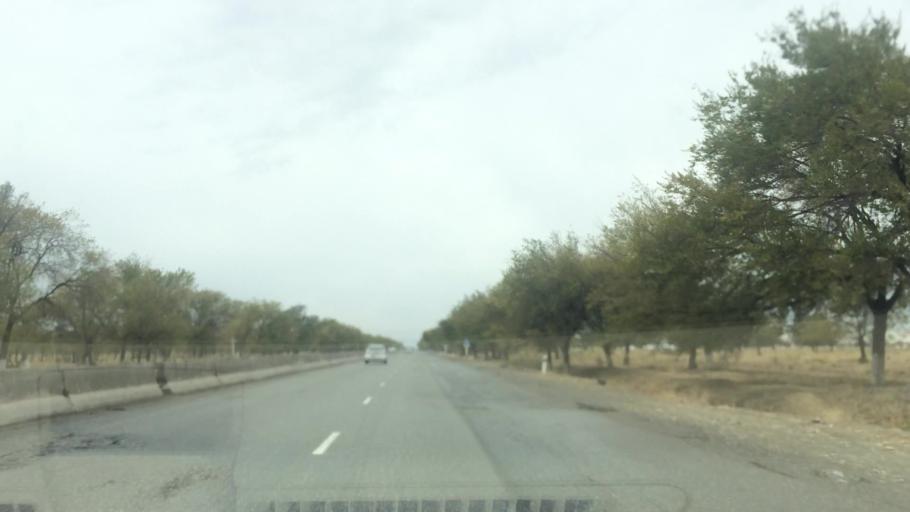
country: UZ
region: Samarqand
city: Bulung'ur
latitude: 39.8098
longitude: 67.3642
